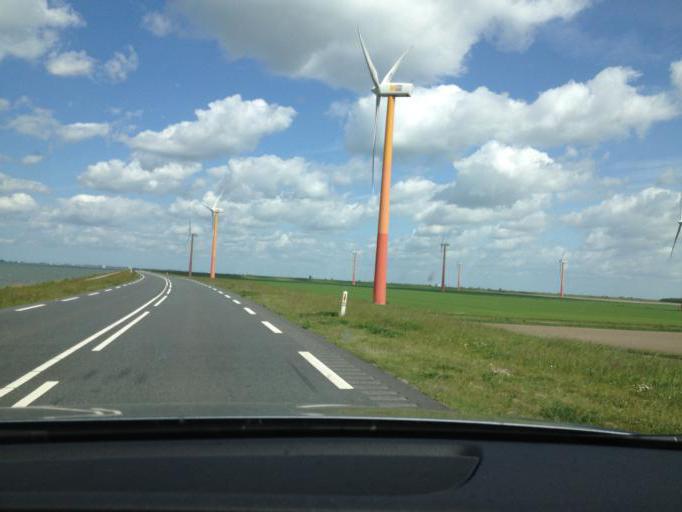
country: NL
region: North Holland
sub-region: Gemeente Naarden
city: Naarden
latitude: 52.3666
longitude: 5.1309
